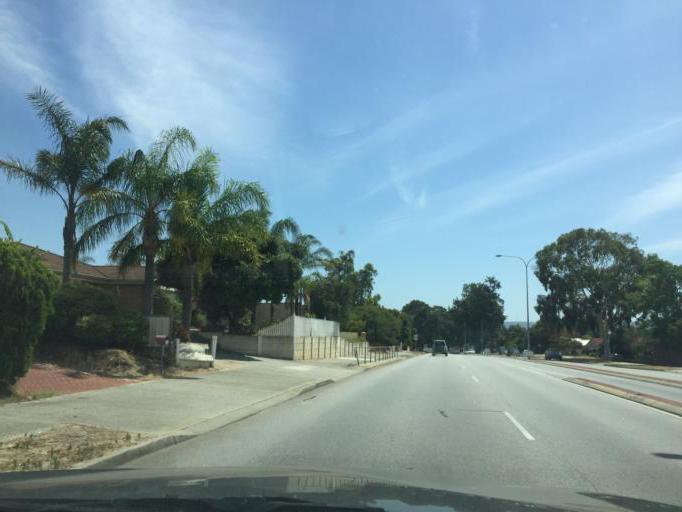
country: AU
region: Western Australia
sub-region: Gosnells
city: Thornlie
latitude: -32.0710
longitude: 115.9664
